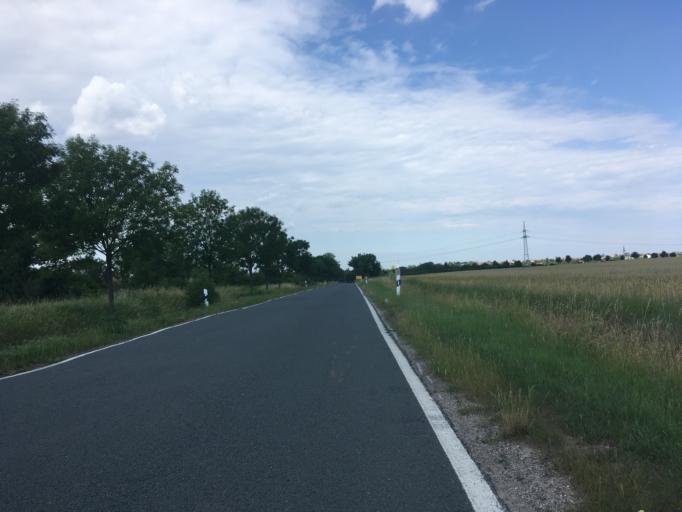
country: DE
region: Saxony-Anhalt
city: Baalberge
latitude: 51.7789
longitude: 11.7838
